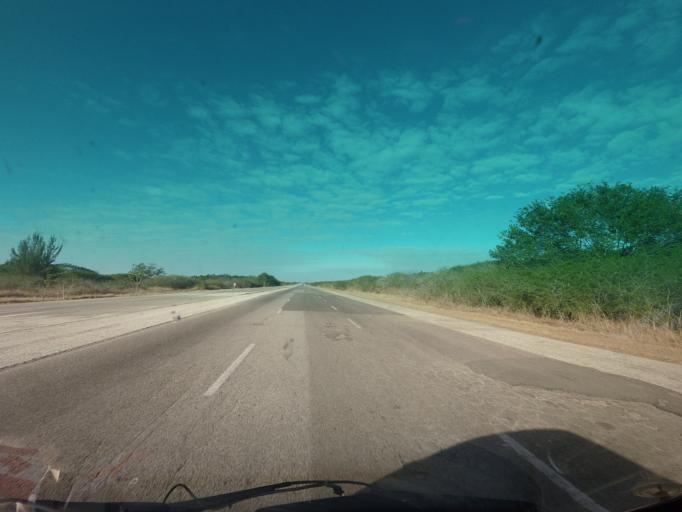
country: CU
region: Cienfuegos
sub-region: Municipio de Aguada de Pasajeros
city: Aguada de Pasajeros
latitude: 22.4361
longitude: -80.7042
